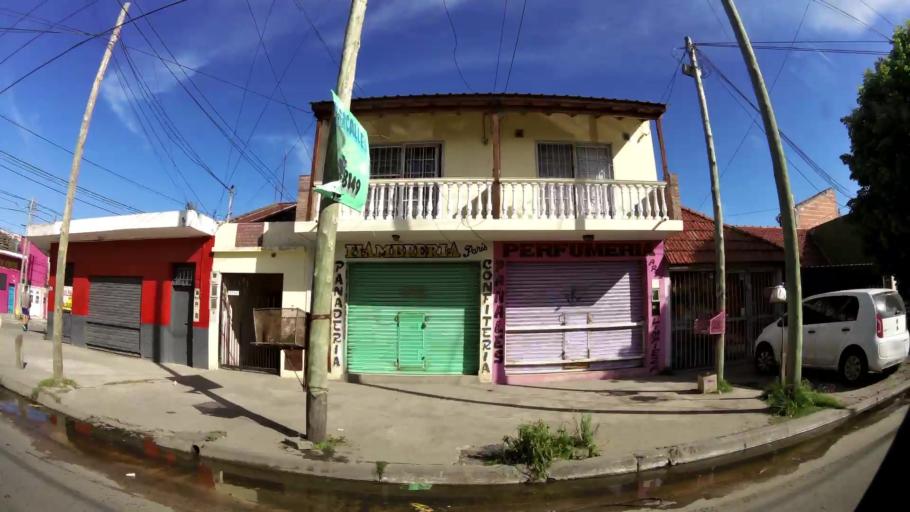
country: AR
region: Buenos Aires
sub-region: Partido de Quilmes
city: Quilmes
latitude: -34.7935
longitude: -58.2337
